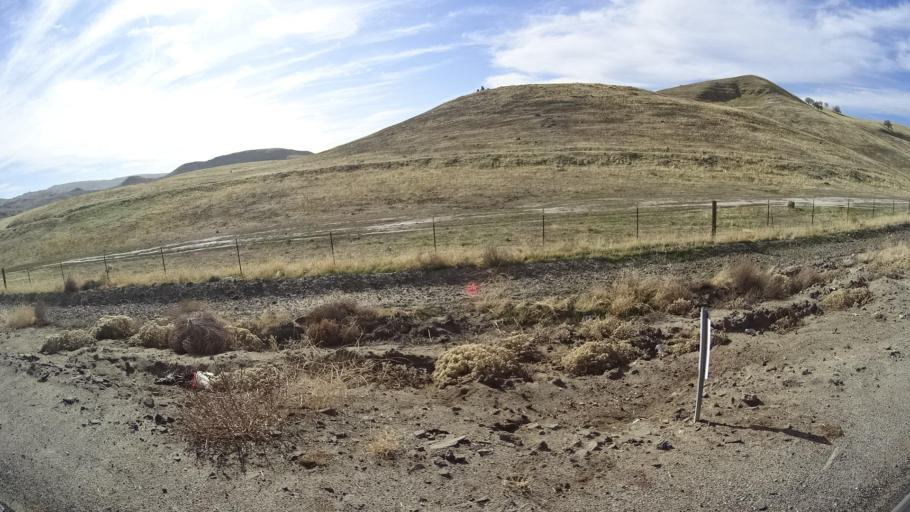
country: US
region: California
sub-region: Kern County
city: Oildale
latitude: 35.6119
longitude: -118.8767
